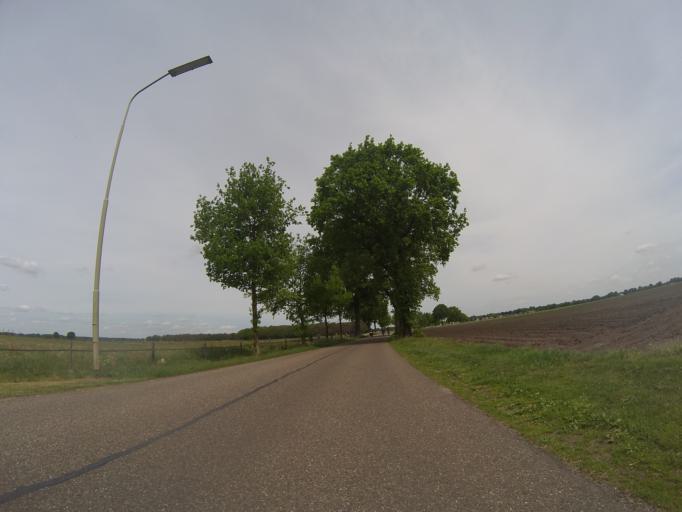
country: NL
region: Drenthe
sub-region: Gemeente Coevorden
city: Sleen
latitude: 52.7795
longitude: 6.8002
